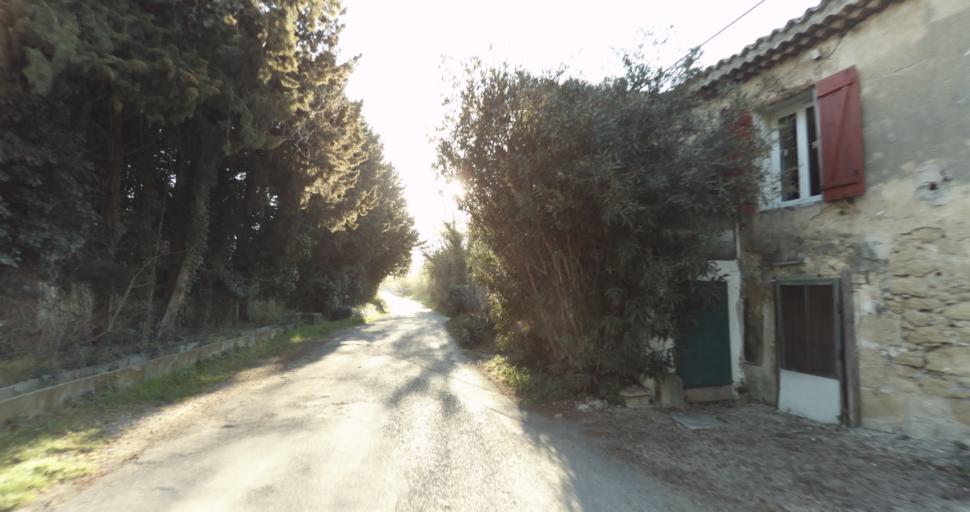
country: FR
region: Provence-Alpes-Cote d'Azur
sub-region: Departement des Bouches-du-Rhone
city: Pelissanne
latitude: 43.6289
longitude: 5.1437
